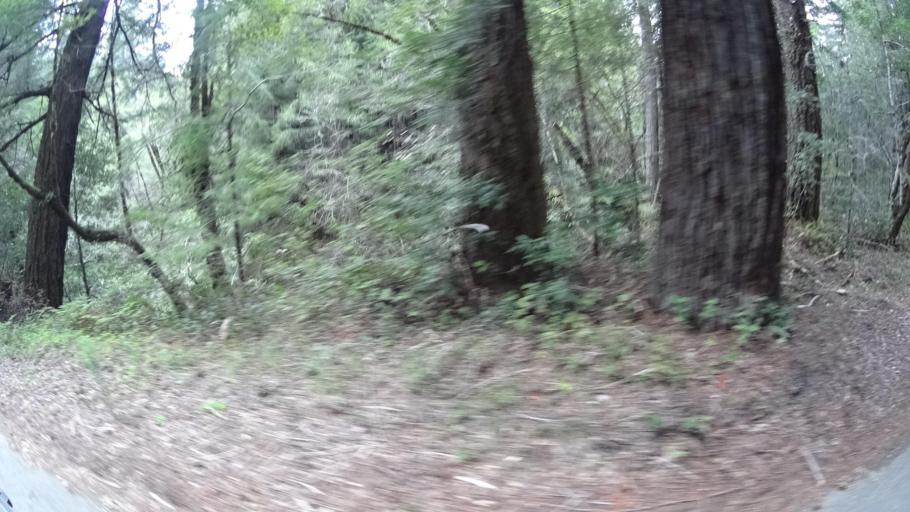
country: US
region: California
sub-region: Humboldt County
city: Redway
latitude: 40.0104
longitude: -123.9301
